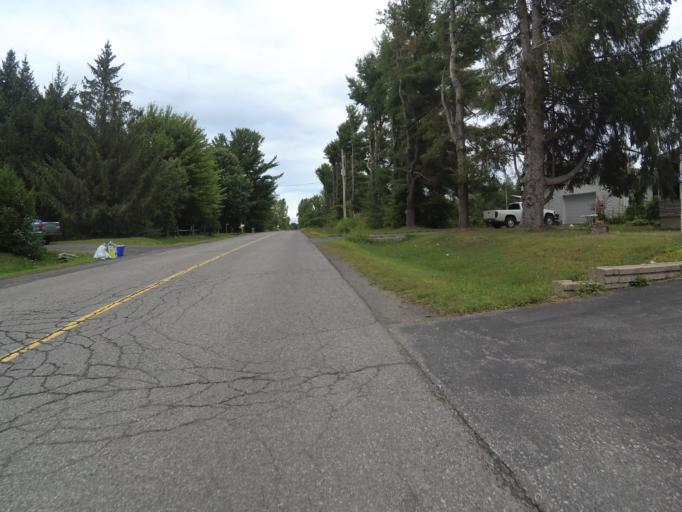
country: CA
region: Ontario
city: Bourget
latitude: 45.4014
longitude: -75.2819
